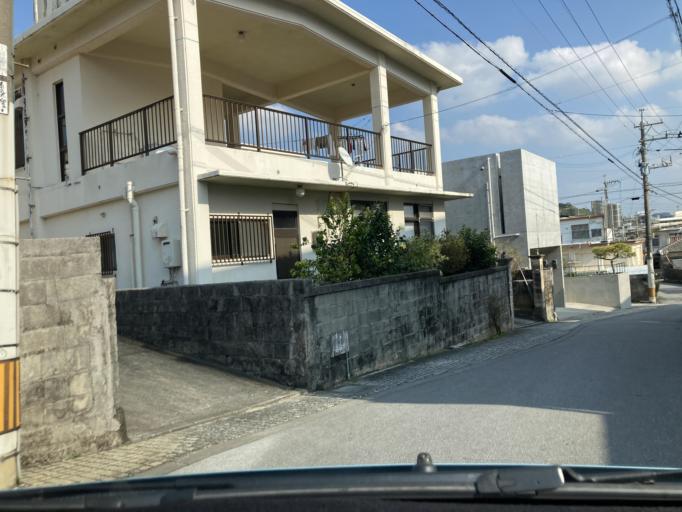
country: JP
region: Okinawa
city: Tomigusuku
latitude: 26.1888
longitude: 127.7248
